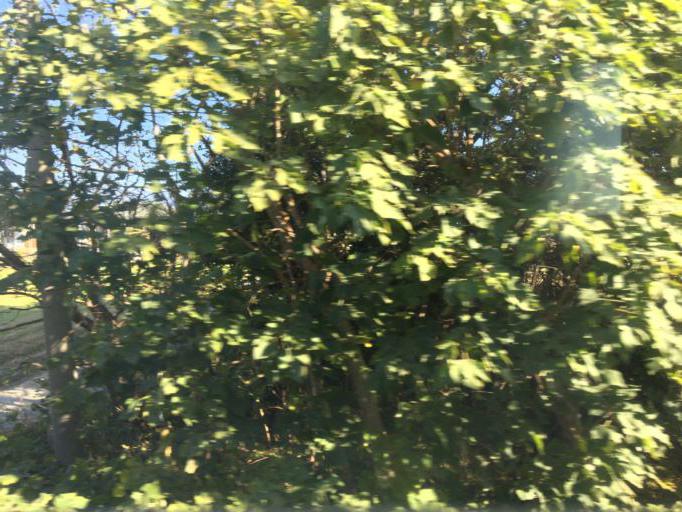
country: JP
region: Gunma
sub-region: Sawa-gun
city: Tamamura
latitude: 36.3637
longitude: 139.1220
